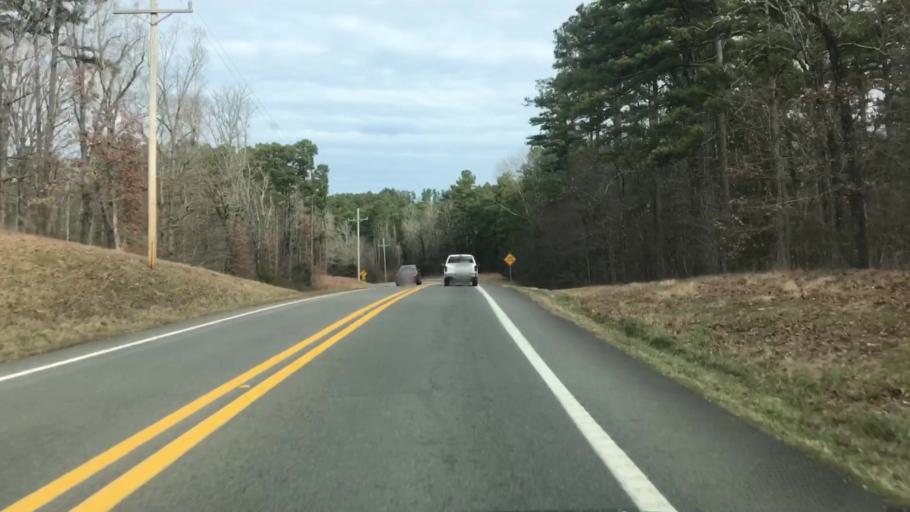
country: US
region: Arkansas
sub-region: Montgomery County
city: Mount Ida
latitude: 34.5897
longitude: -93.6642
